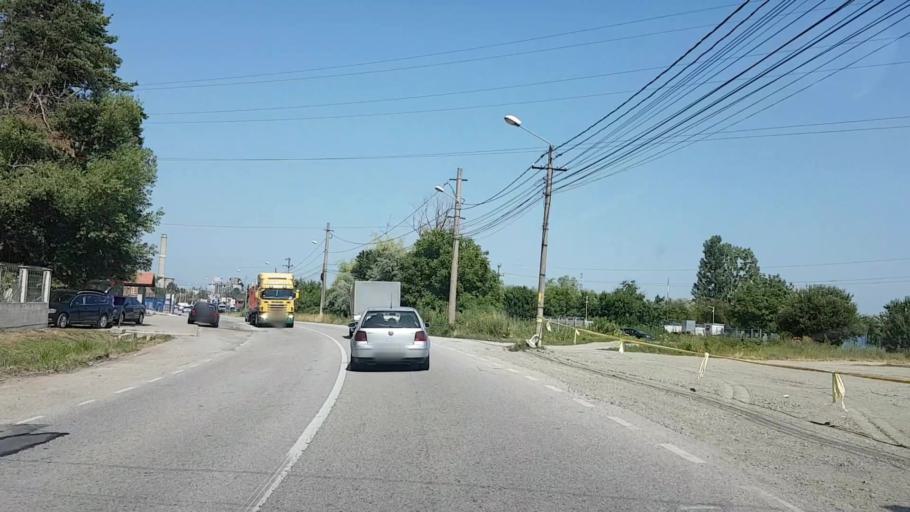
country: RO
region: Cluj
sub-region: Municipiul Dej
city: Dej
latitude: 47.1558
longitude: 23.8814
